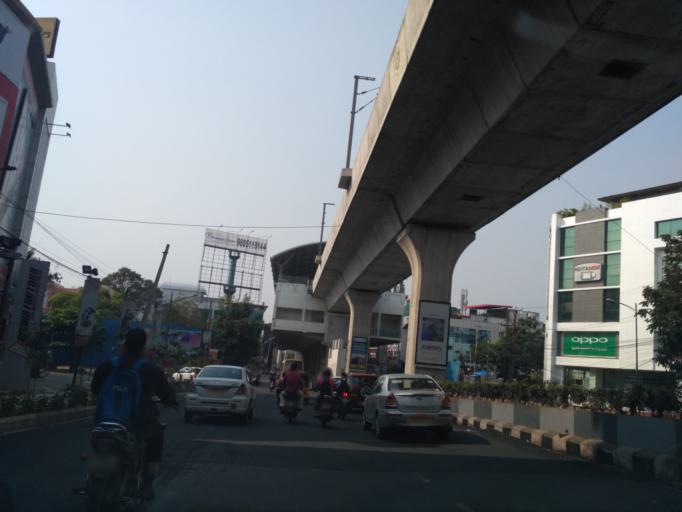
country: IN
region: Telangana
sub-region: Rangareddi
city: Kukatpalli
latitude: 17.4361
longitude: 78.4011
